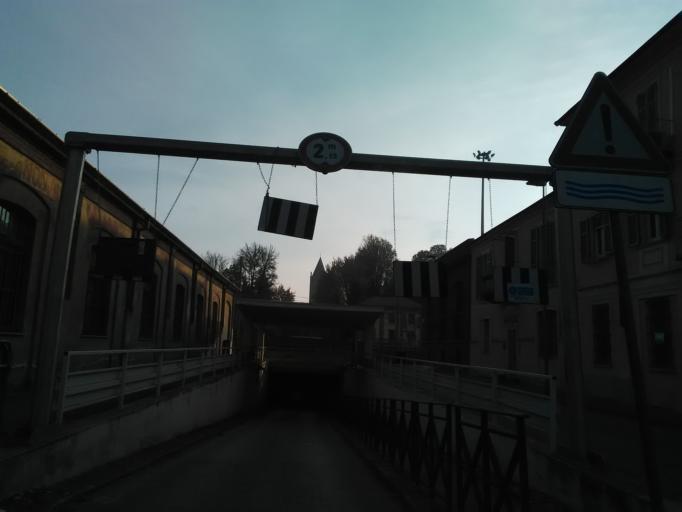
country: IT
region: Piedmont
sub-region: Provincia di Vercelli
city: Vercelli
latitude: 45.3320
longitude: 8.4204
